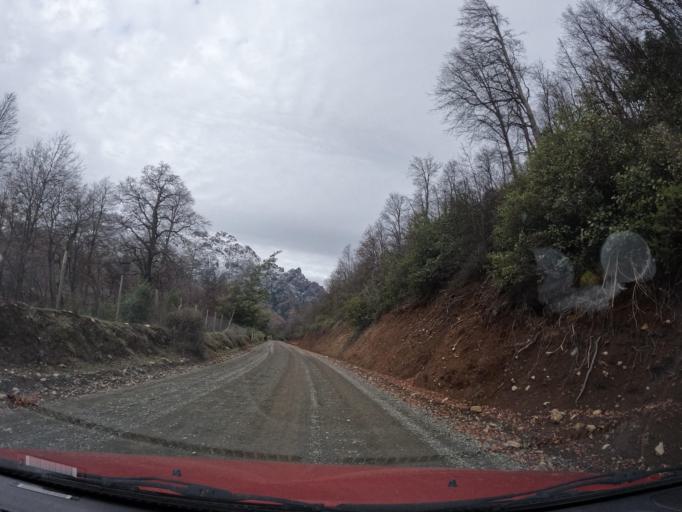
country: CL
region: Maule
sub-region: Provincia de Linares
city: Colbun
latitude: -35.8583
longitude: -71.1480
